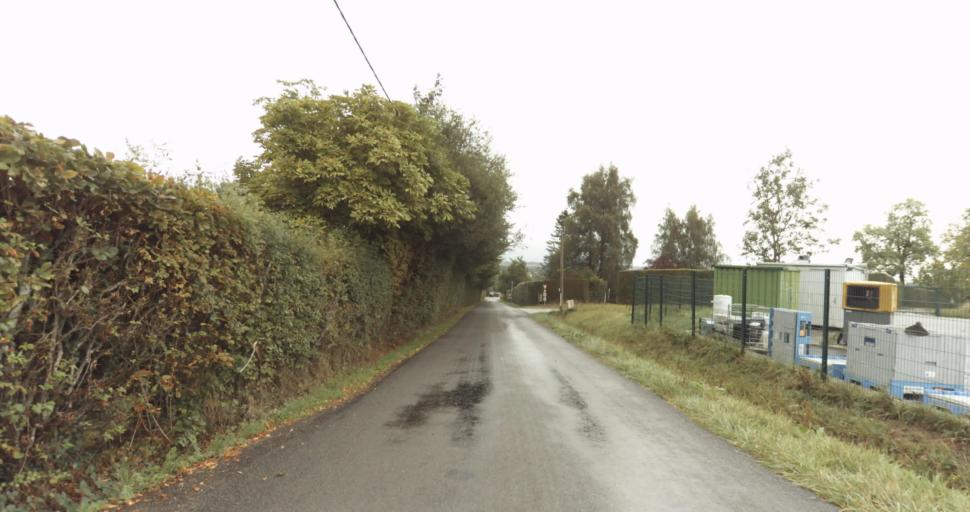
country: FR
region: Lower Normandy
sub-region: Departement de l'Orne
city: Sainte-Gauburge-Sainte-Colombe
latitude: 48.7149
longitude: 0.4379
